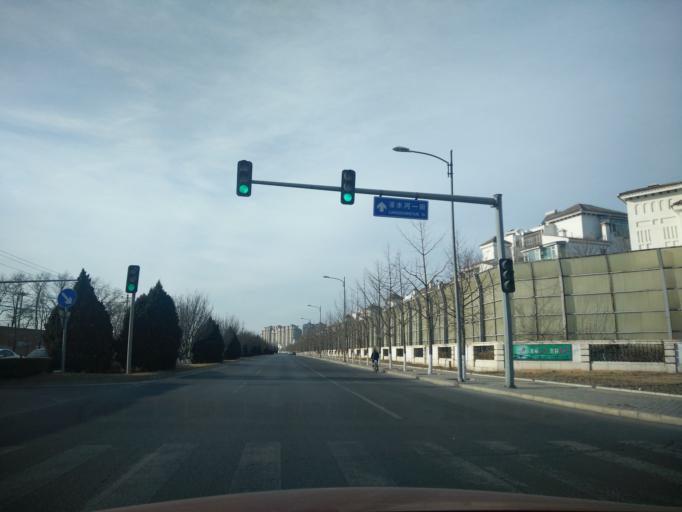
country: CN
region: Beijing
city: Jiugong
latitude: 39.7741
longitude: 116.4864
